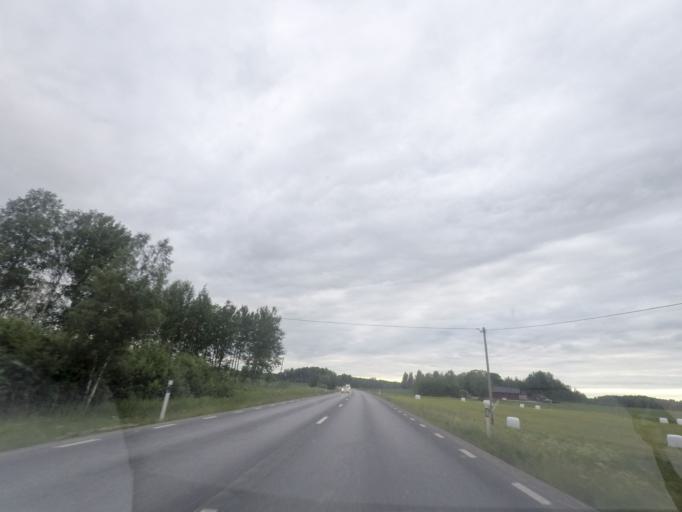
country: SE
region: OErebro
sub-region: Lindesbergs Kommun
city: Lindesberg
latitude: 59.5448
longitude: 15.2452
